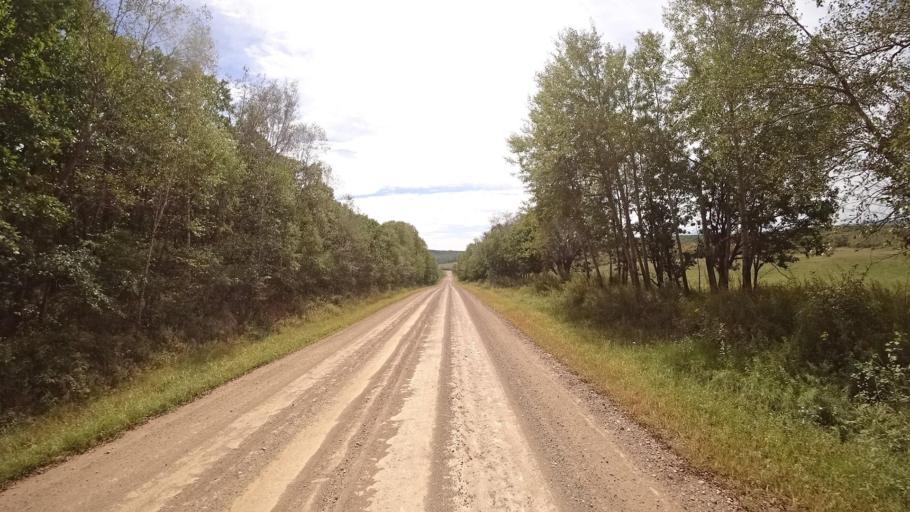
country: RU
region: Primorskiy
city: Yakovlevka
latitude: 44.6248
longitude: 133.5995
